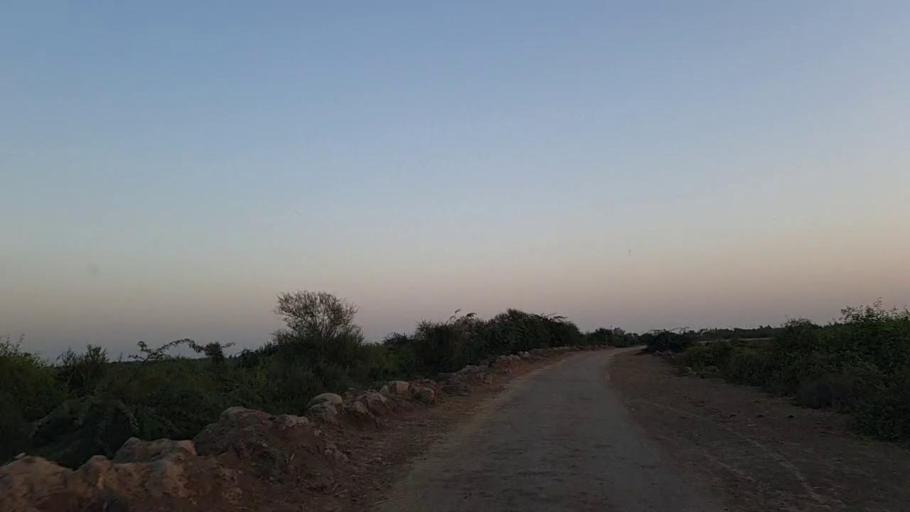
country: PK
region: Sindh
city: Mirpur Batoro
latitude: 24.6257
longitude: 68.1844
